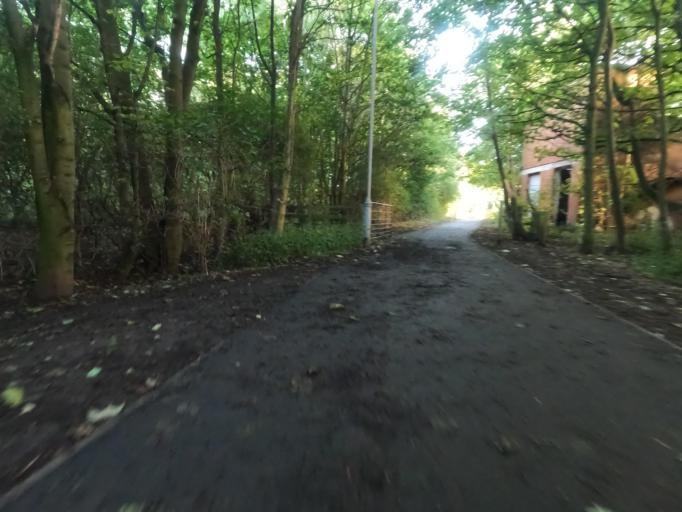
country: GB
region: England
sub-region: Northumberland
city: Seaton Delaval
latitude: 55.0797
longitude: -1.5341
